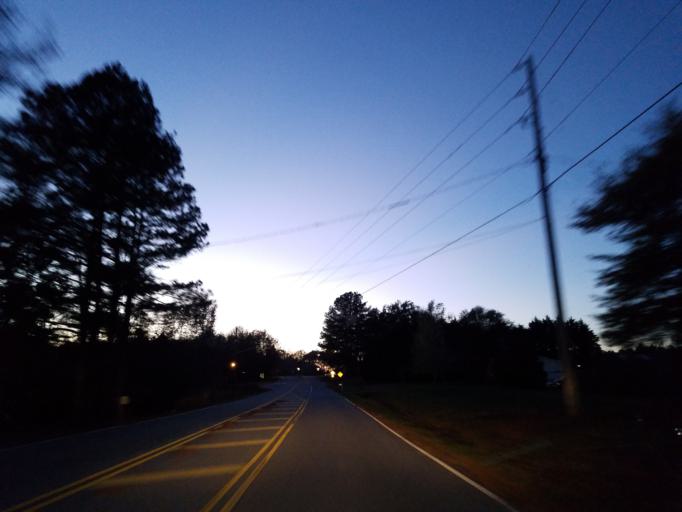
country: US
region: Georgia
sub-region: Dawson County
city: Dawsonville
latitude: 34.3234
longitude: -84.0708
